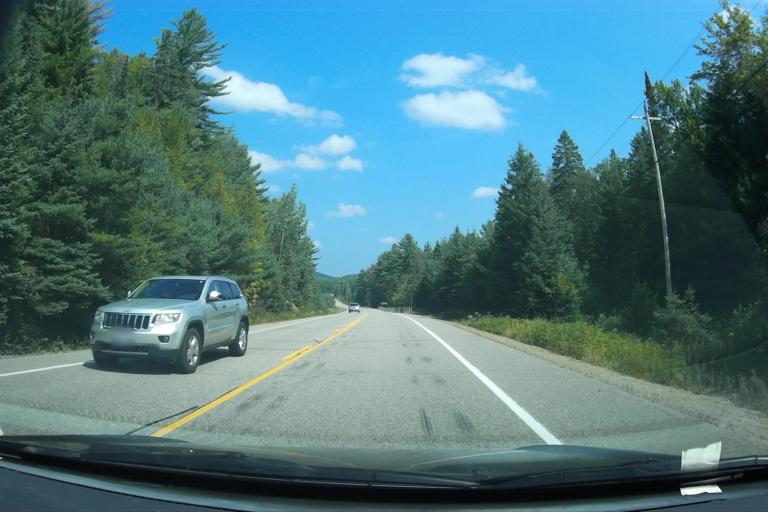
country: CA
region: Ontario
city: Huntsville
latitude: 45.5715
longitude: -78.5291
